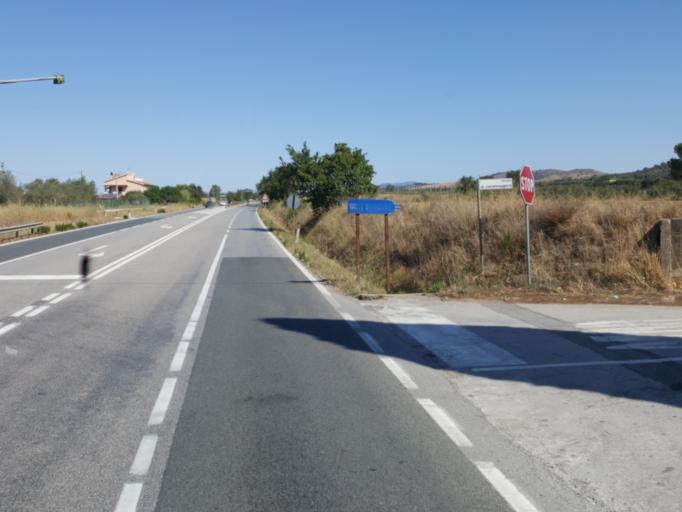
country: IT
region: Tuscany
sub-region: Provincia di Grosseto
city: Grosseto
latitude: 42.6892
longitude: 11.1386
